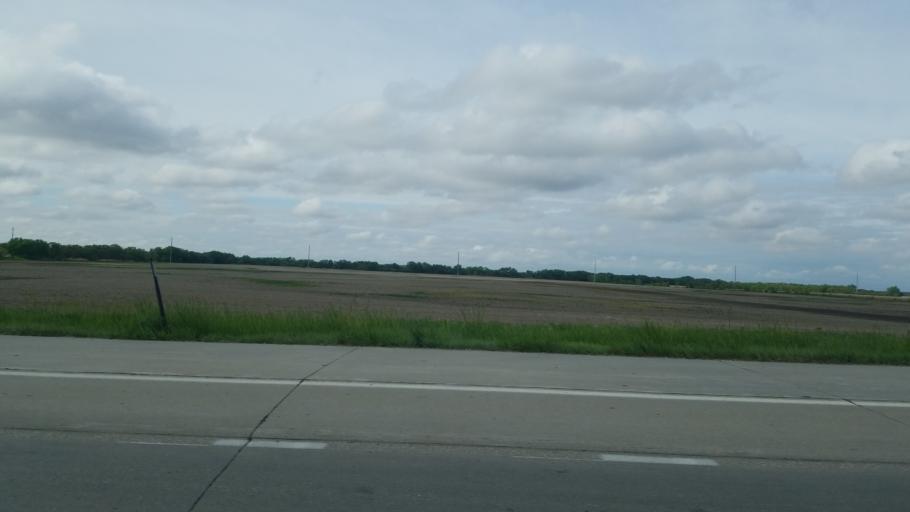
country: US
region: Nebraska
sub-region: Lancaster County
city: Waverly
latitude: 40.8978
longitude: -96.5731
